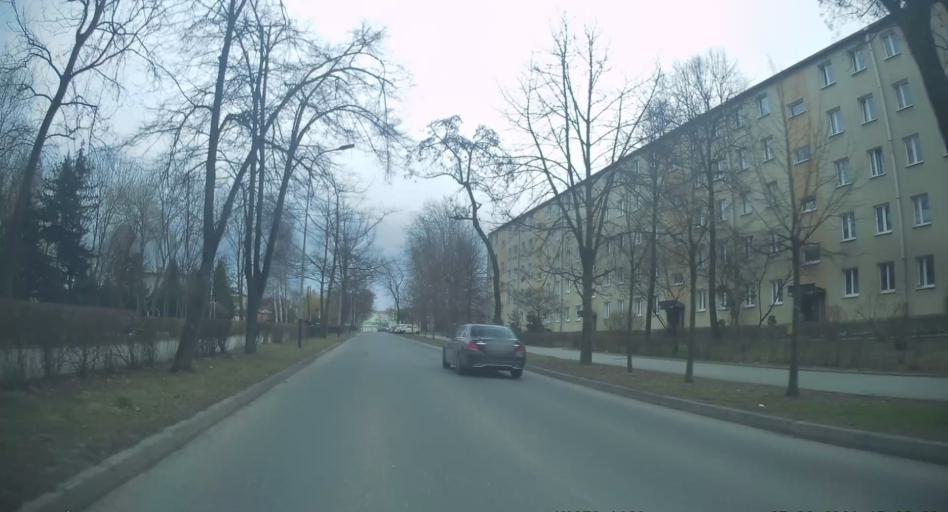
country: PL
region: Lesser Poland Voivodeship
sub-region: Krakow
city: Krakow
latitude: 50.0204
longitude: 19.9799
